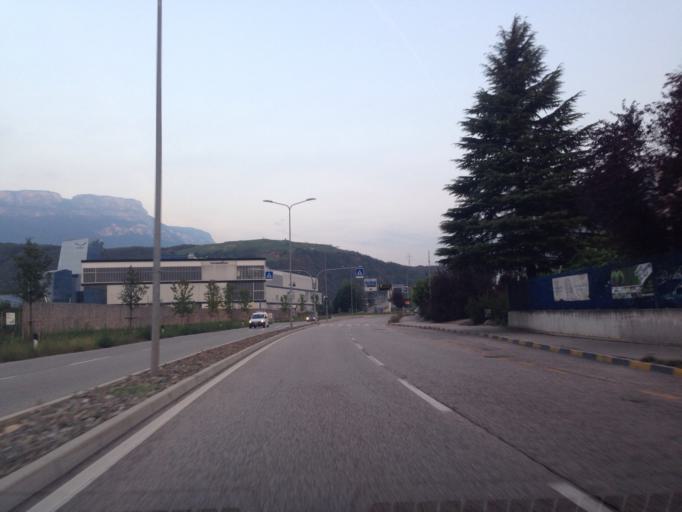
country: IT
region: Trentino-Alto Adige
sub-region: Bolzano
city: San Giacomo
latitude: 46.4700
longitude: 11.3188
